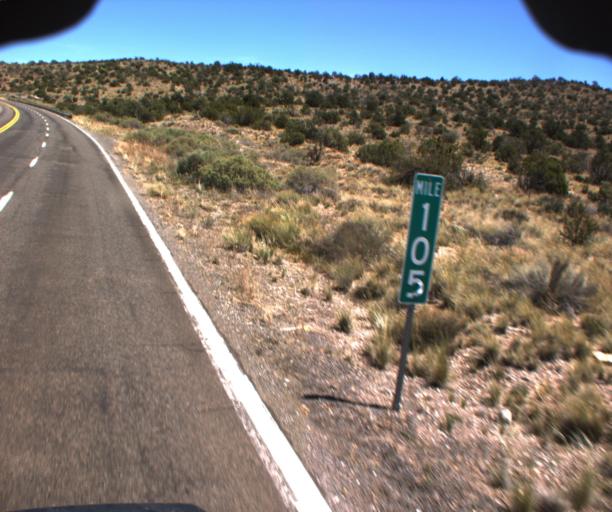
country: US
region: Arizona
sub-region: Mohave County
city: Peach Springs
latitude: 35.5421
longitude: -113.4064
